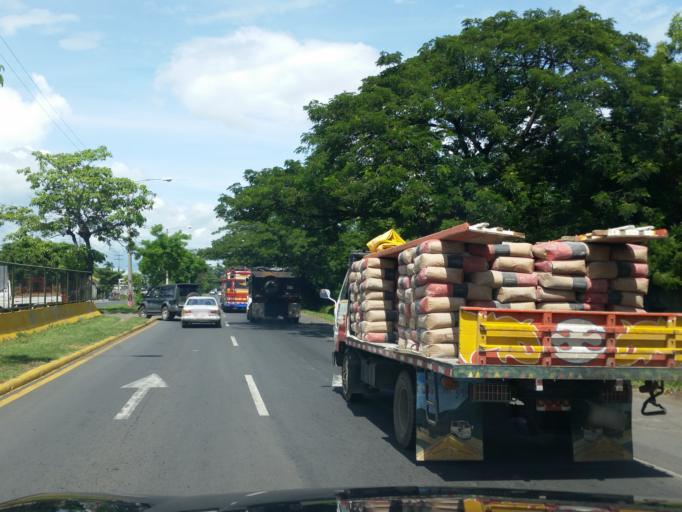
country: NI
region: Managua
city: Tipitapa
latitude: 12.1503
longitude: -86.1548
